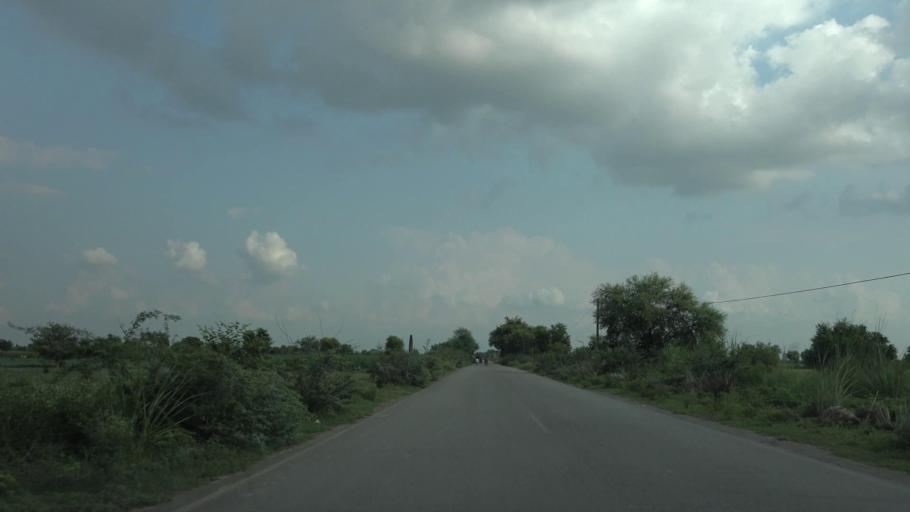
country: PK
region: Punjab
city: Nankana Sahib
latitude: 31.4898
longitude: 73.6063
